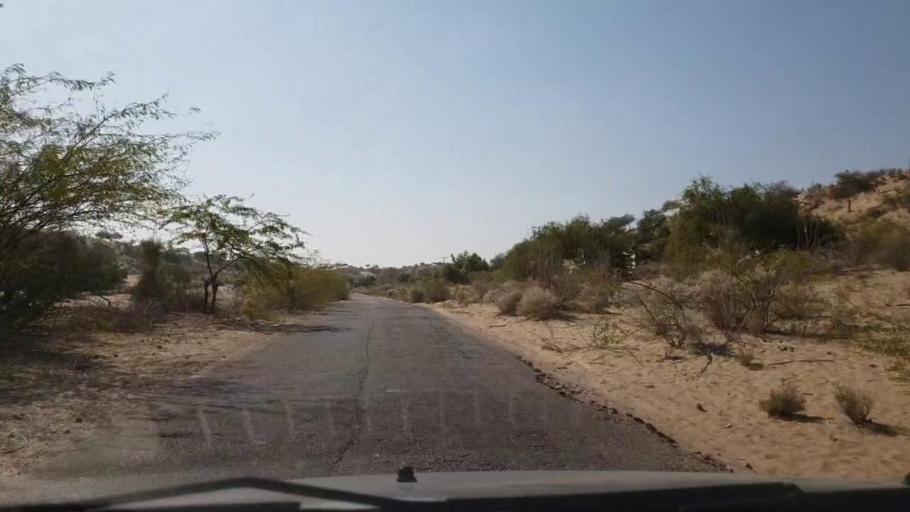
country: PK
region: Sindh
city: Diplo
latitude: 24.5458
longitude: 69.6502
